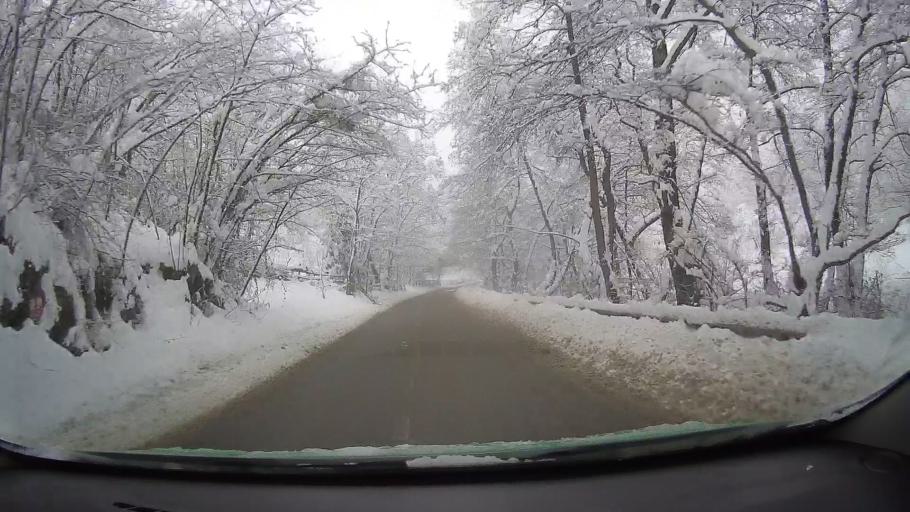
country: RO
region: Sibiu
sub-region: Comuna Tilisca
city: Tilisca
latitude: 45.8031
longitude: 23.8322
